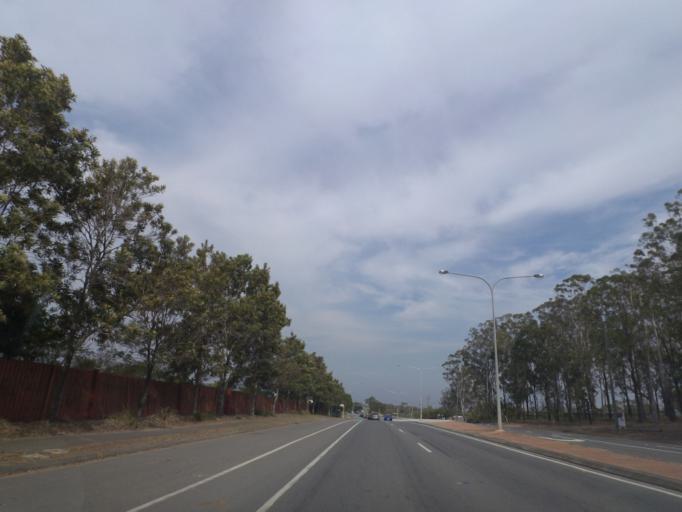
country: AU
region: Queensland
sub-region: Brisbane
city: Sunnybank
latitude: -27.5971
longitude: 153.0257
